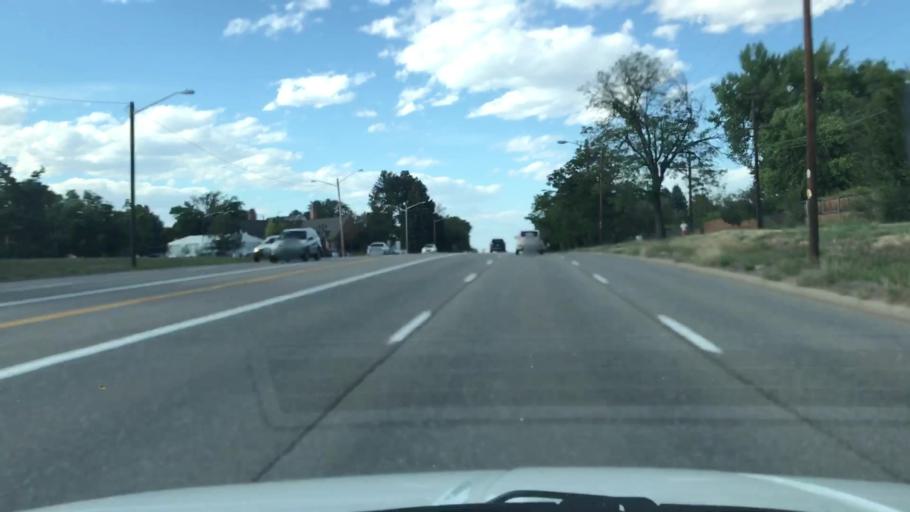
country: US
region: Colorado
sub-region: Arapahoe County
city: Cherry Hills Village
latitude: 39.6563
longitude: -104.9405
